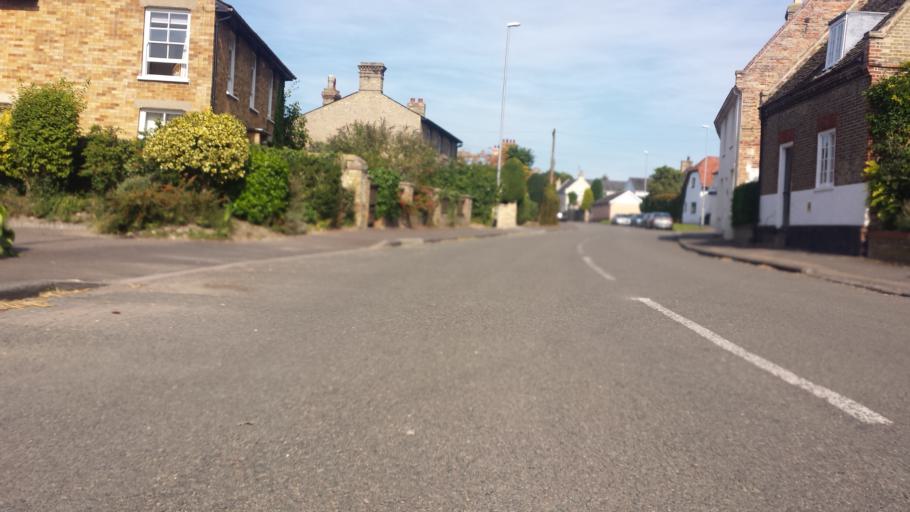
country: GB
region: England
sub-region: Cambridgeshire
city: Bottisham
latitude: 52.2527
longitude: 0.2958
